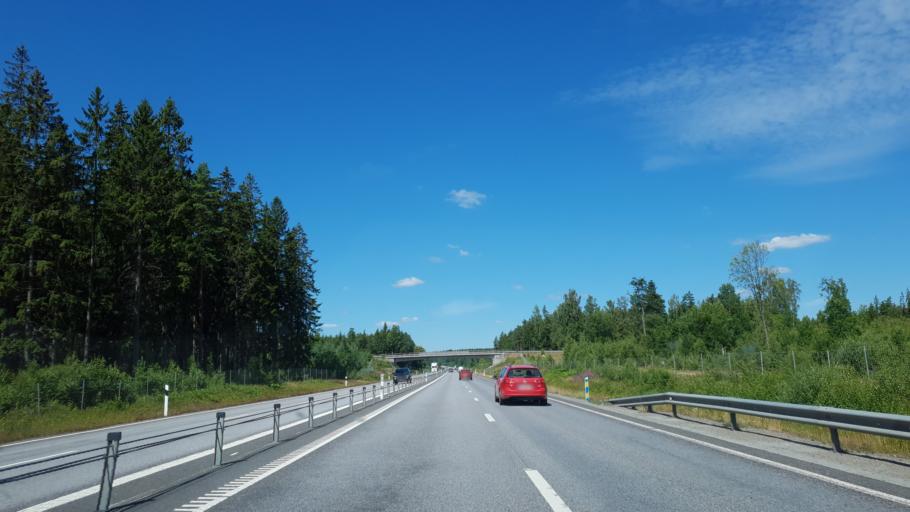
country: SE
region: Kronoberg
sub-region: Vaxjo Kommun
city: Gemla
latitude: 56.9121
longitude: 14.6333
